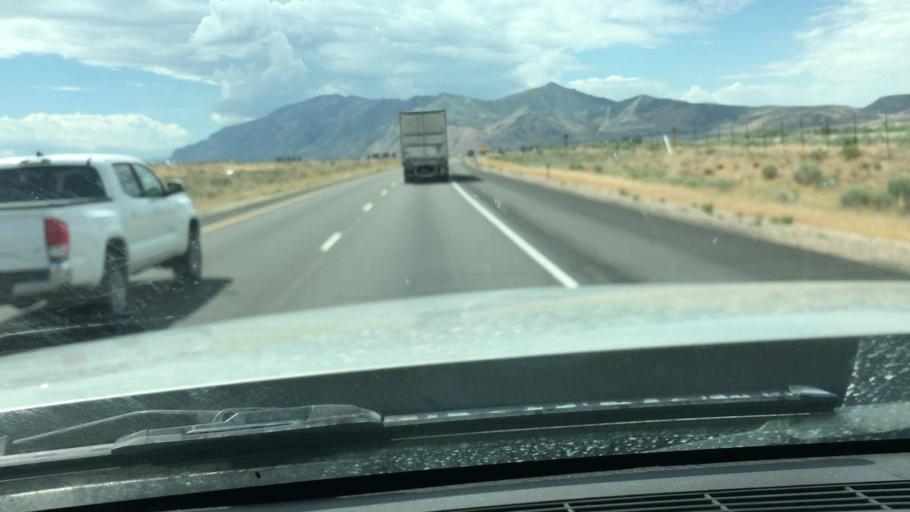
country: US
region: Utah
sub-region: Sanpete County
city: Gunnison
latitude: 39.2786
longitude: -112.0940
